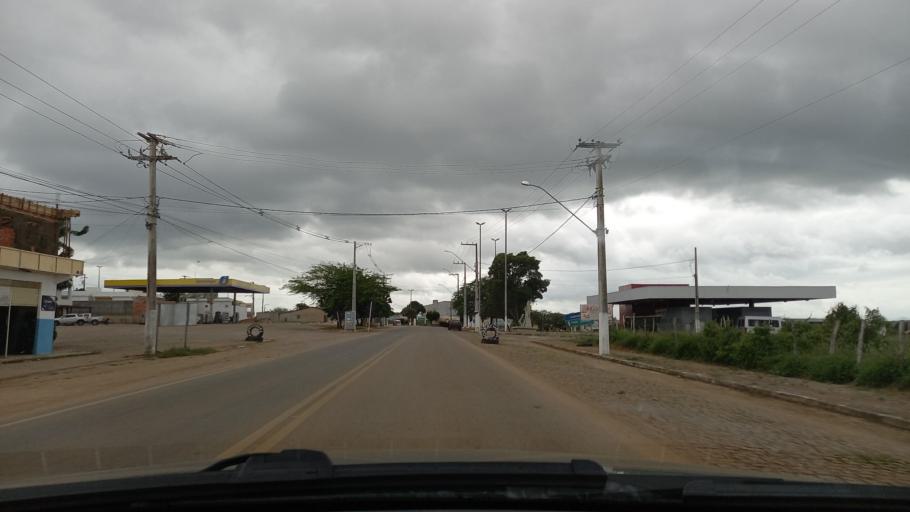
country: BR
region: Sergipe
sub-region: Caninde De Sao Francisco
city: Caninde de Sao Francisco
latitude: -9.6676
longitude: -37.7970
